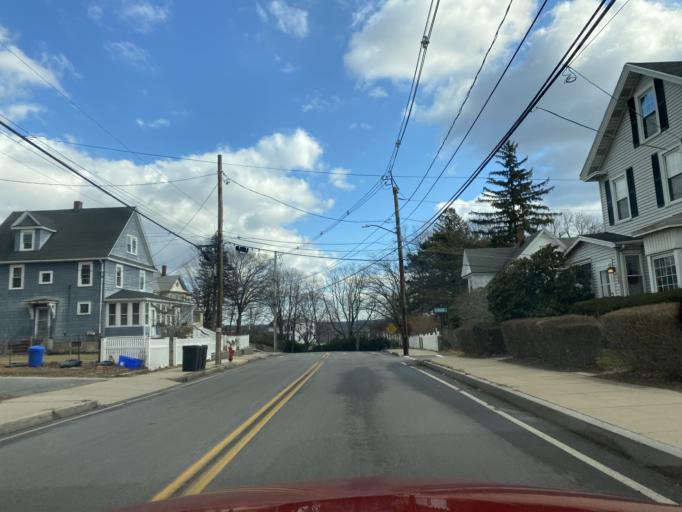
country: US
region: Massachusetts
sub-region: Middlesex County
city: Woburn
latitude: 42.4821
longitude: -71.1382
